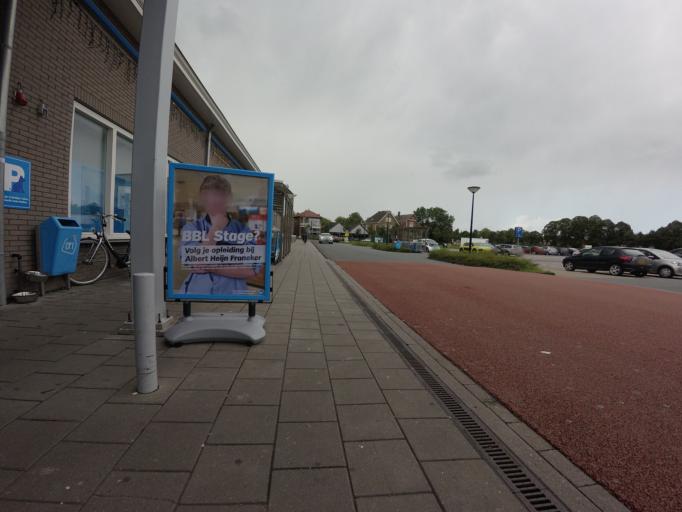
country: NL
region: Friesland
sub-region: Gemeente Franekeradeel
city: Franeker
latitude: 53.1878
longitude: 5.5505
